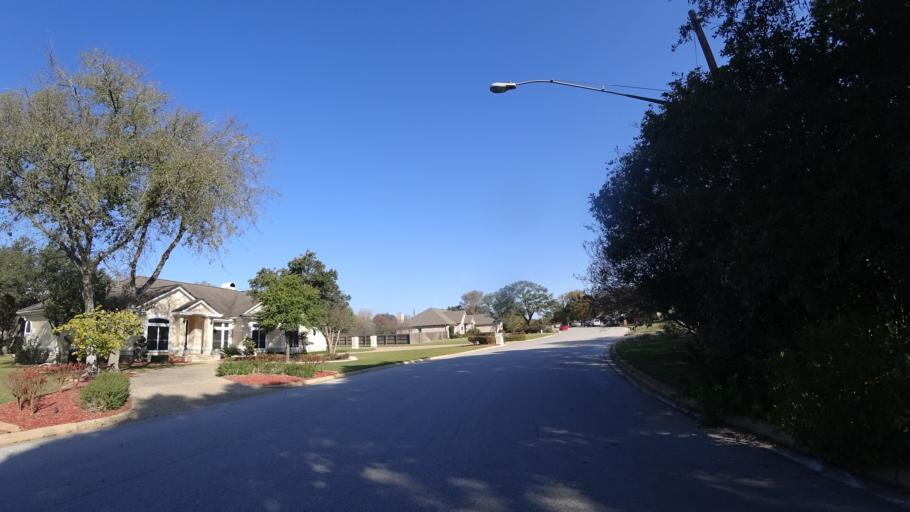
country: US
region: Texas
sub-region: Travis County
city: Shady Hollow
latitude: 30.2231
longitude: -97.8501
